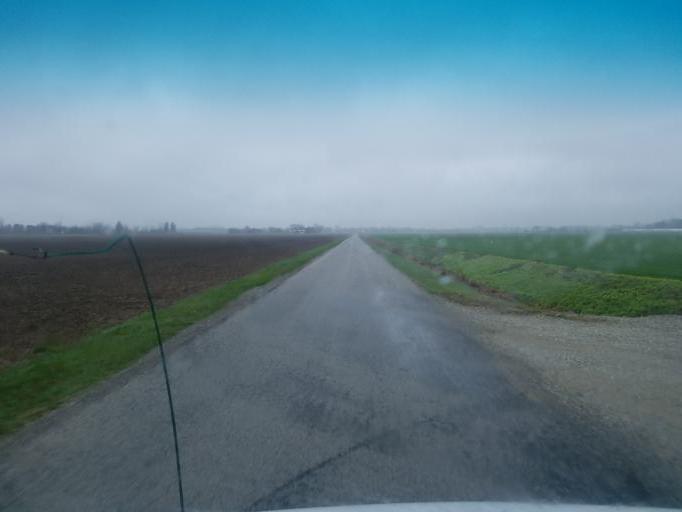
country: US
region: Ohio
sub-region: Wood County
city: North Baltimore
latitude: 41.2610
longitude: -83.6312
